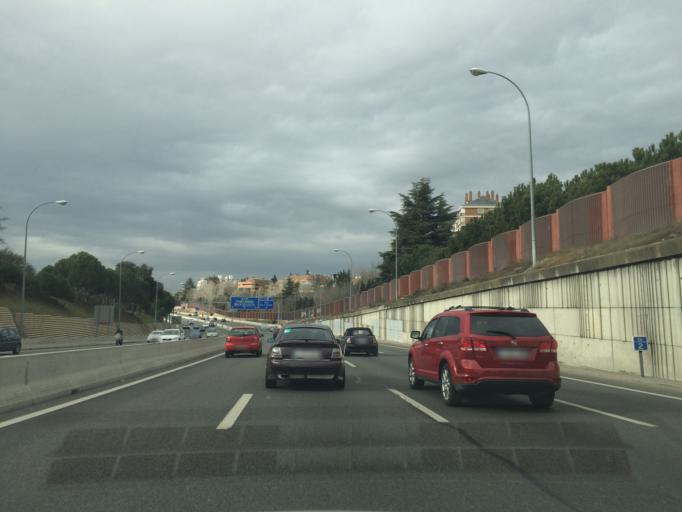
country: ES
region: Madrid
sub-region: Provincia de Madrid
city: Tetuan de las Victorias
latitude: 40.4741
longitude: -3.7396
